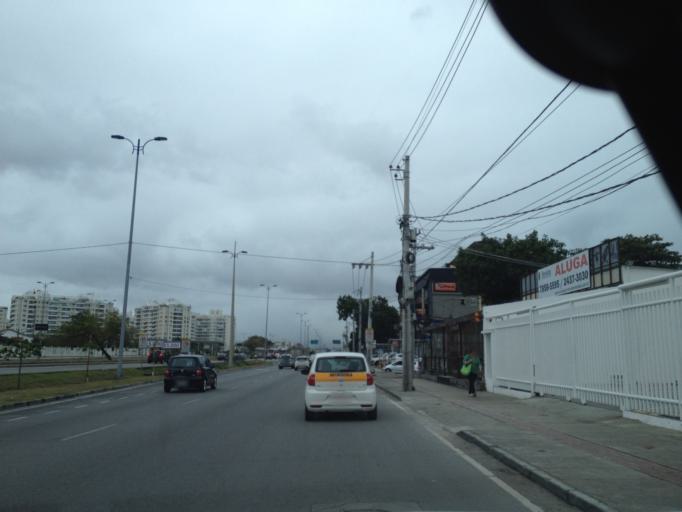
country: BR
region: Rio de Janeiro
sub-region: Nilopolis
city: Nilopolis
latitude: -23.0121
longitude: -43.4567
